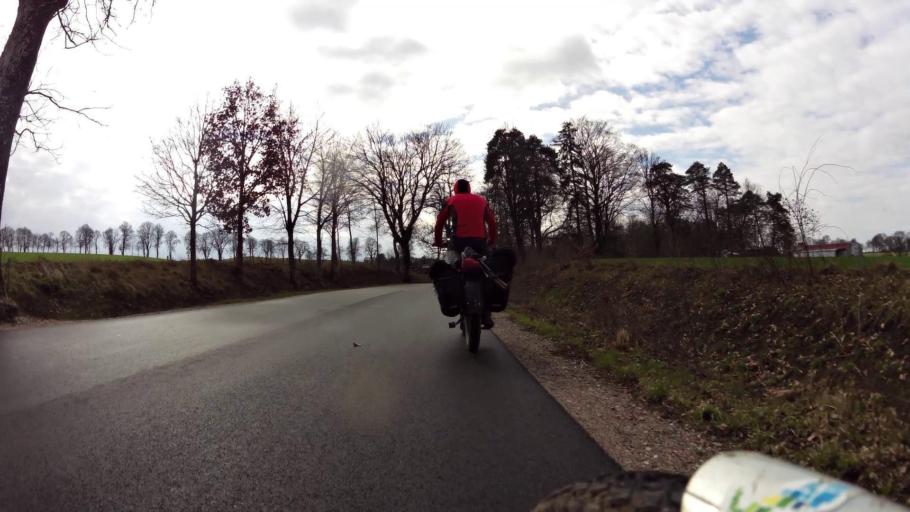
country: PL
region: Pomeranian Voivodeship
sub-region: Powiat bytowski
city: Kolczyglowy
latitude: 54.2214
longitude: 17.2393
